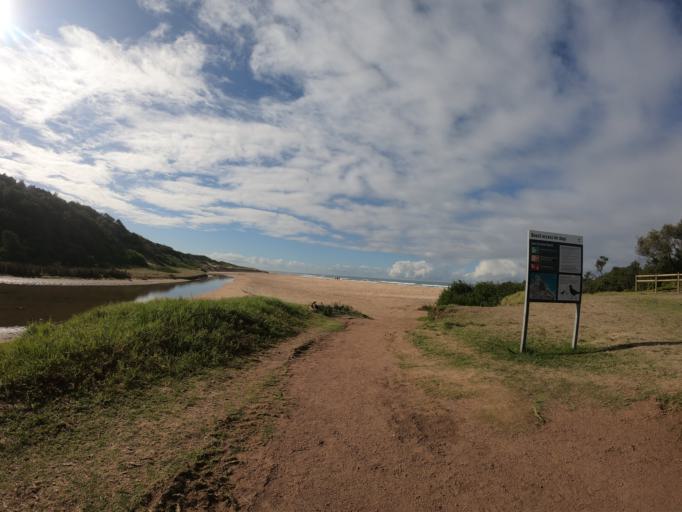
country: AU
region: New South Wales
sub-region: Wollongong
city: East Corrimal
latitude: -34.3767
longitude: 150.9201
